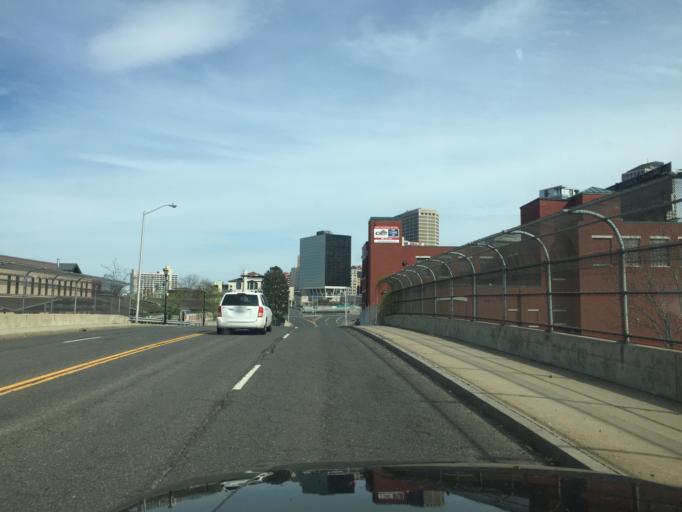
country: US
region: Connecticut
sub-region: Hartford County
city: Hartford
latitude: 41.7725
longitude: -72.6811
